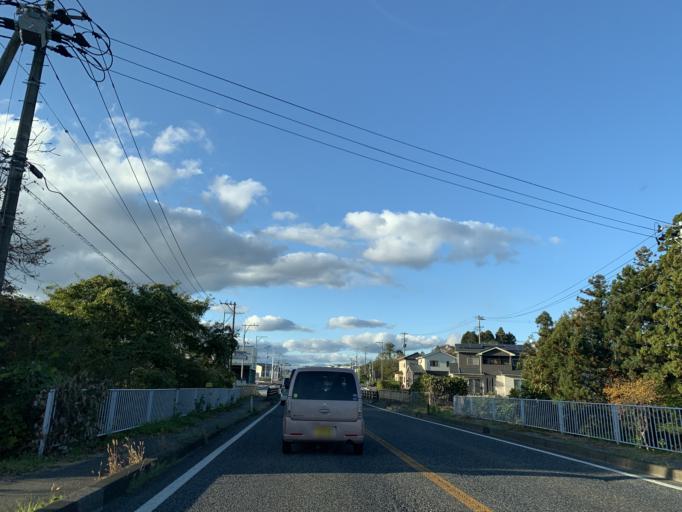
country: JP
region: Iwate
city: Kitakami
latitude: 39.2233
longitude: 141.0969
